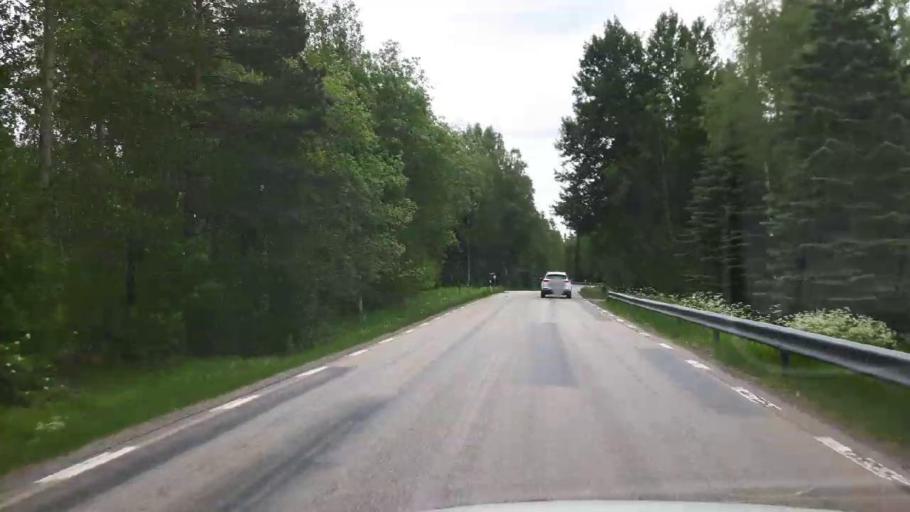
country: SE
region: Vaestmanland
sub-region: Norbergs Kommun
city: Norberg
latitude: 60.1123
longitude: 15.9188
